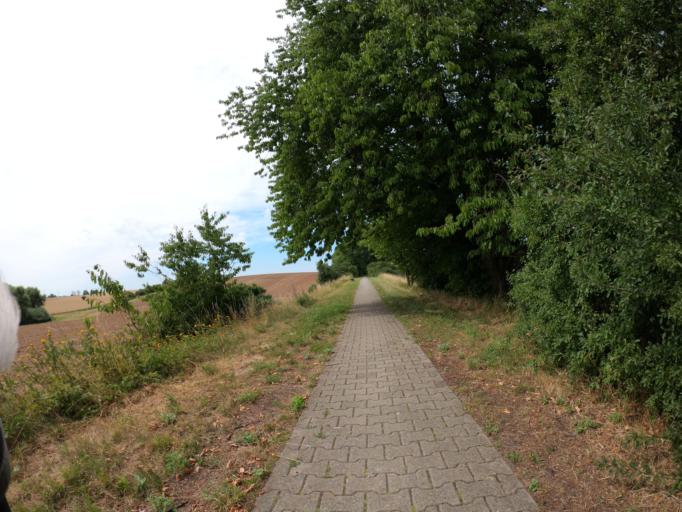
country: DE
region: Mecklenburg-Vorpommern
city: Woldegk
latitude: 53.4531
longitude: 13.5588
